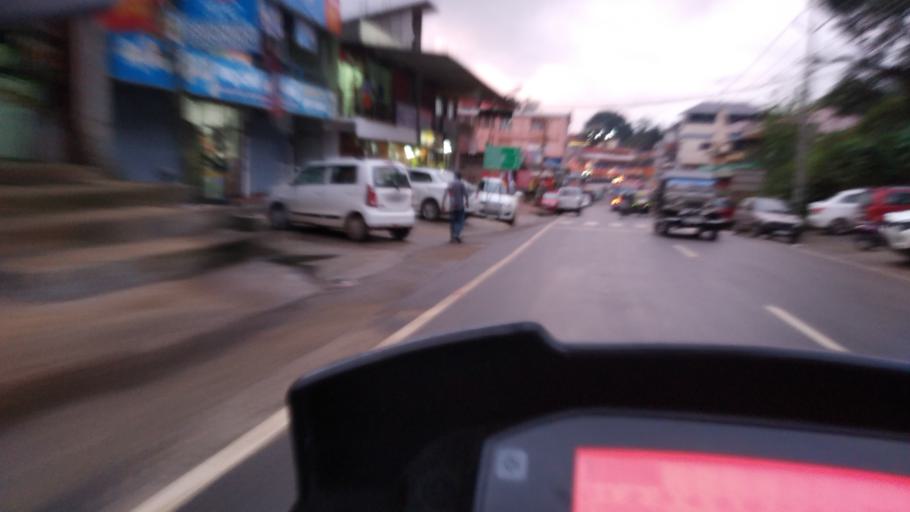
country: IN
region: Kerala
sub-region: Idukki
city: Munnar
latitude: 9.9627
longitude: 77.0995
